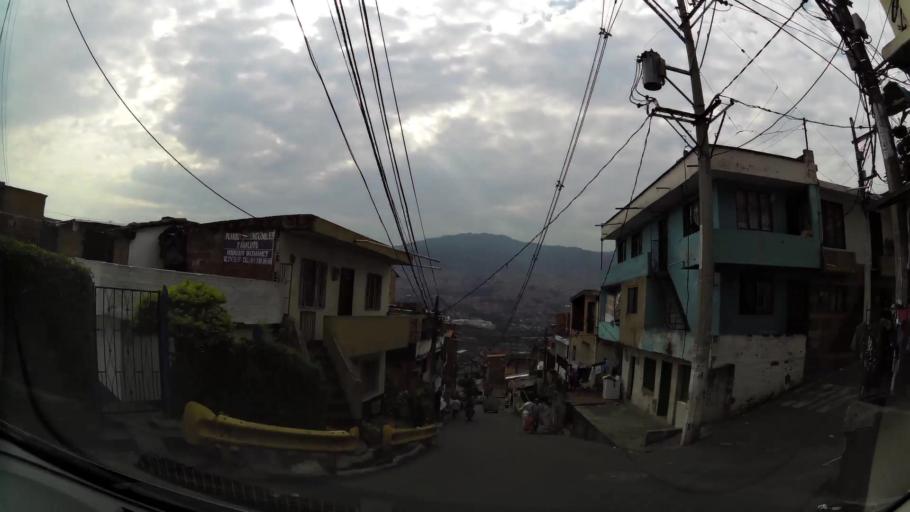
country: CO
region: Antioquia
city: Bello
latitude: 6.2998
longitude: -75.5501
